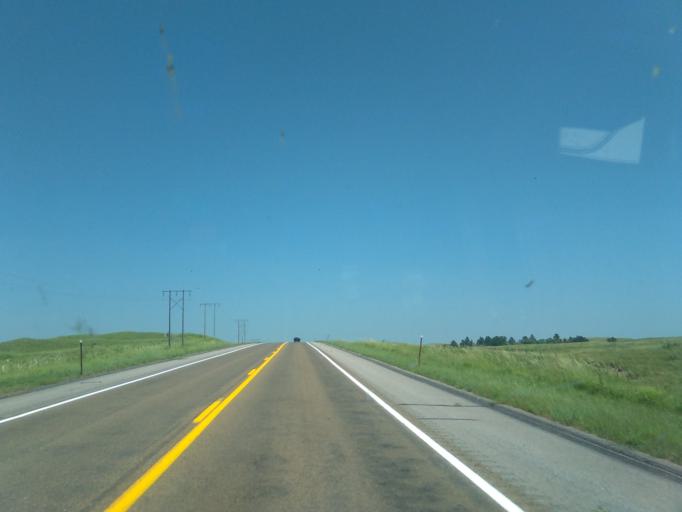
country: US
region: Nebraska
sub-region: Lincoln County
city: North Platte
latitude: 40.8901
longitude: -100.7540
